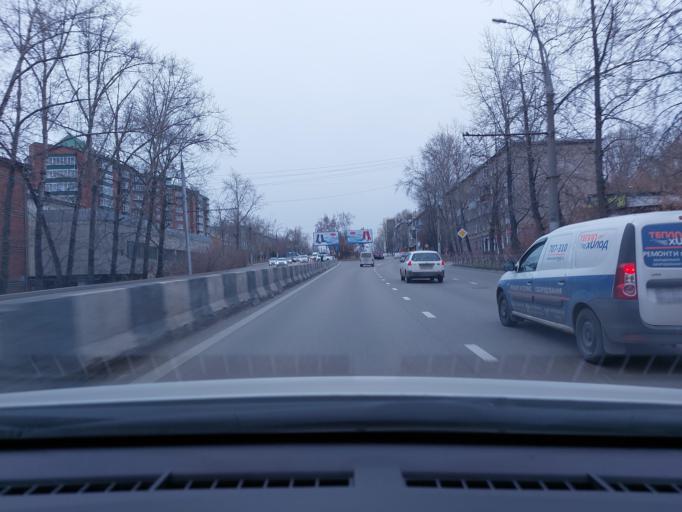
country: RU
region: Irkutsk
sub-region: Irkutskiy Rayon
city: Irkutsk
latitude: 52.2661
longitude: 104.2582
